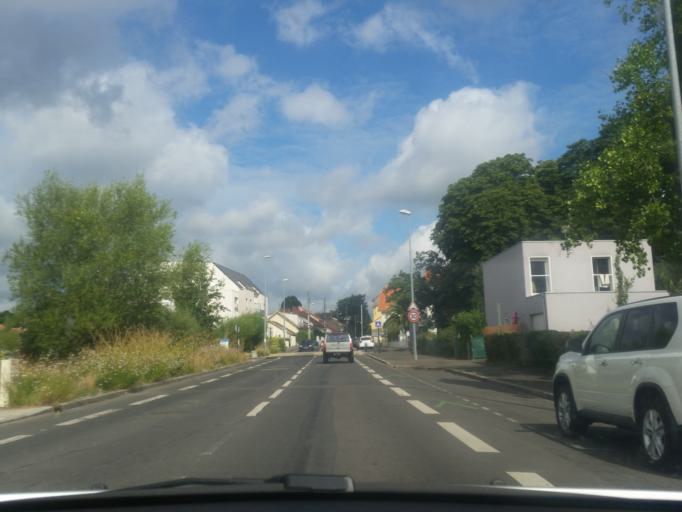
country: FR
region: Pays de la Loire
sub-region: Departement de la Loire-Atlantique
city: Saint-Sebastien-sur-Loire
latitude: 47.2358
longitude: -1.5221
